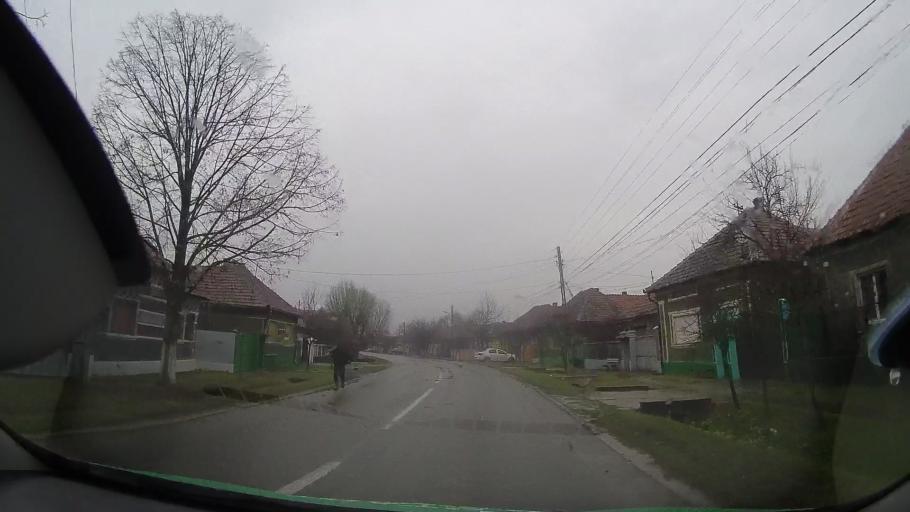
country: RO
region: Bihor
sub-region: Comuna Tulca
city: Tulca
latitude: 46.7910
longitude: 21.7717
